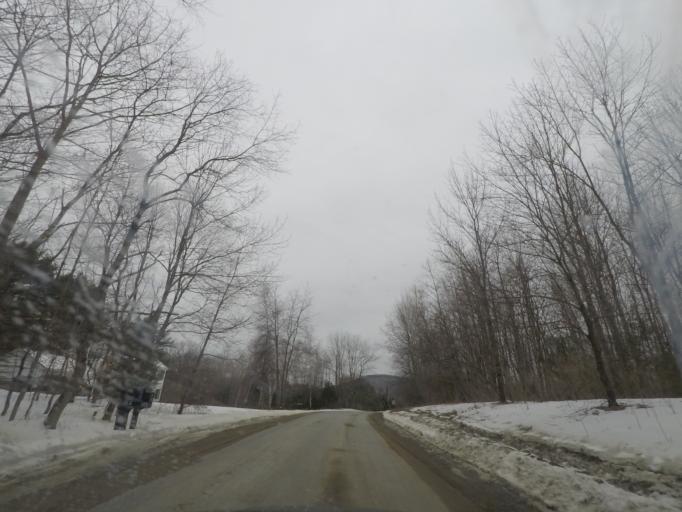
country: US
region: Massachusetts
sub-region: Berkshire County
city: Richmond
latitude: 42.5400
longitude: -73.4087
